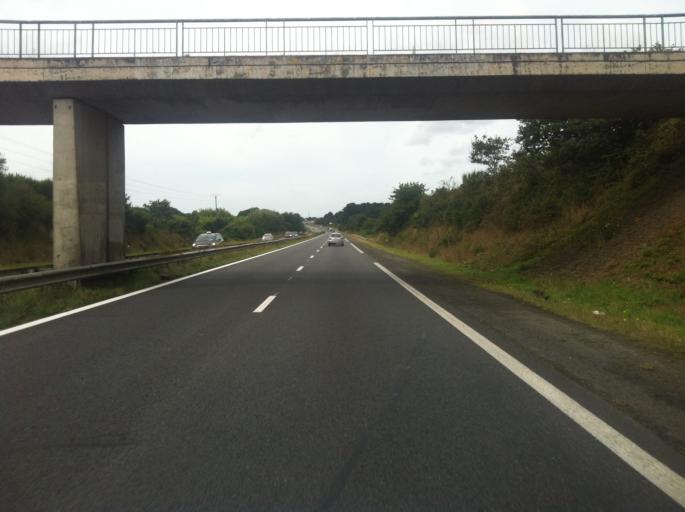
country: FR
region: Brittany
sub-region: Departement du Finistere
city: Guipavas
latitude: 48.4495
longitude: -4.3864
